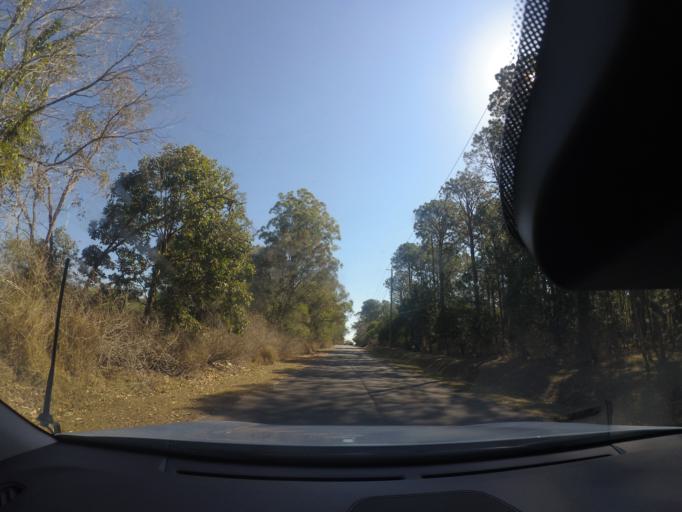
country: AU
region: Queensland
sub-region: Logan
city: Woodridge
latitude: -27.6414
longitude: 153.0917
